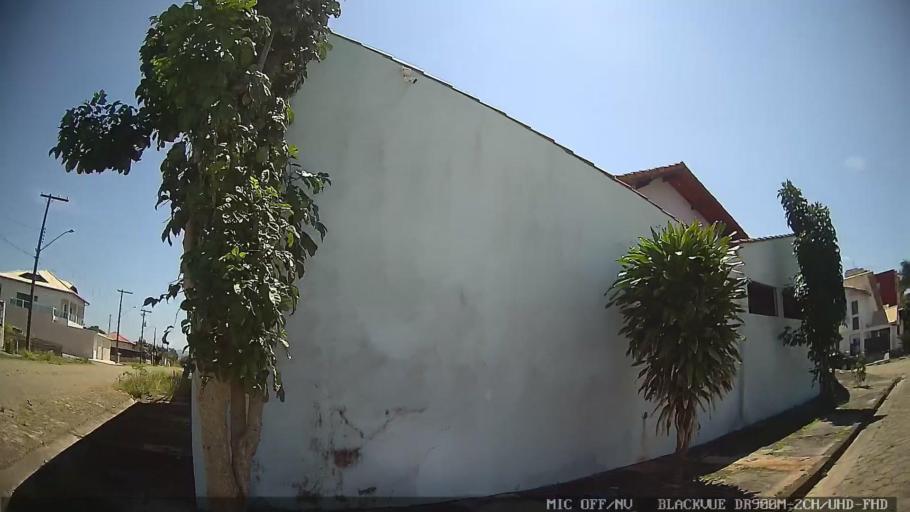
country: BR
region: Sao Paulo
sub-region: Peruibe
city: Peruibe
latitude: -24.2990
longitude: -46.9741
